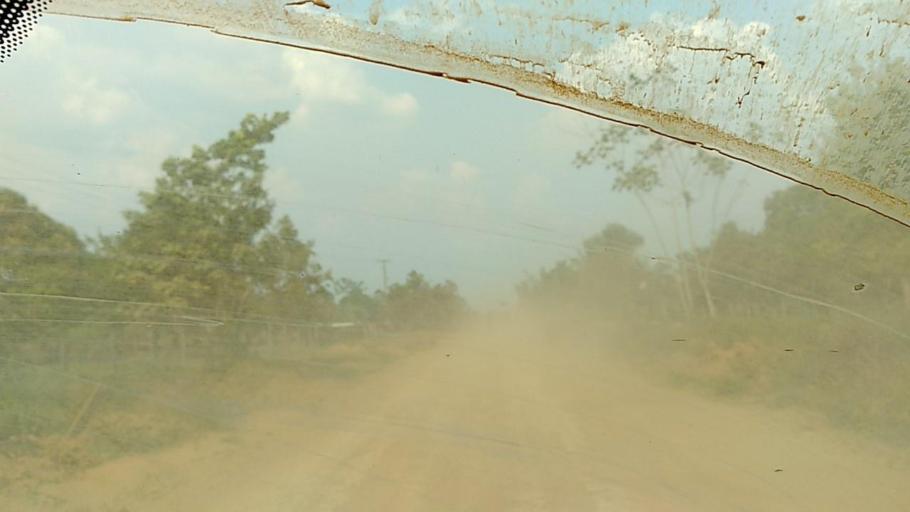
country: BR
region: Rondonia
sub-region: Porto Velho
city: Porto Velho
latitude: -8.6836
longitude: -63.2277
